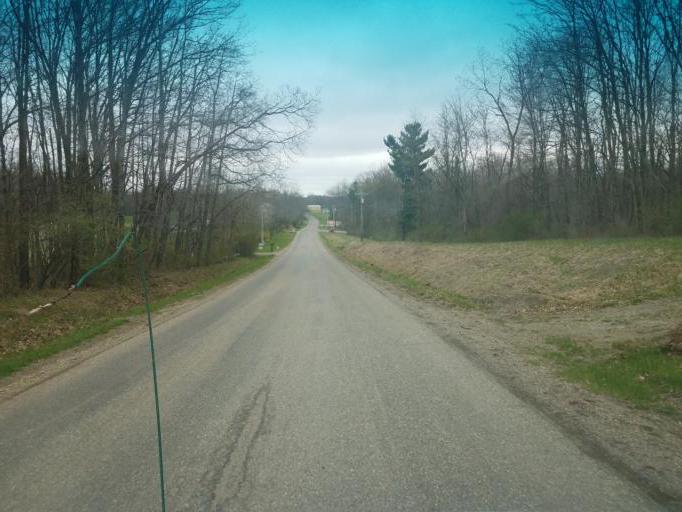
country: US
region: Ohio
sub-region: Stark County
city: Beach City
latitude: 40.6315
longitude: -81.6139
